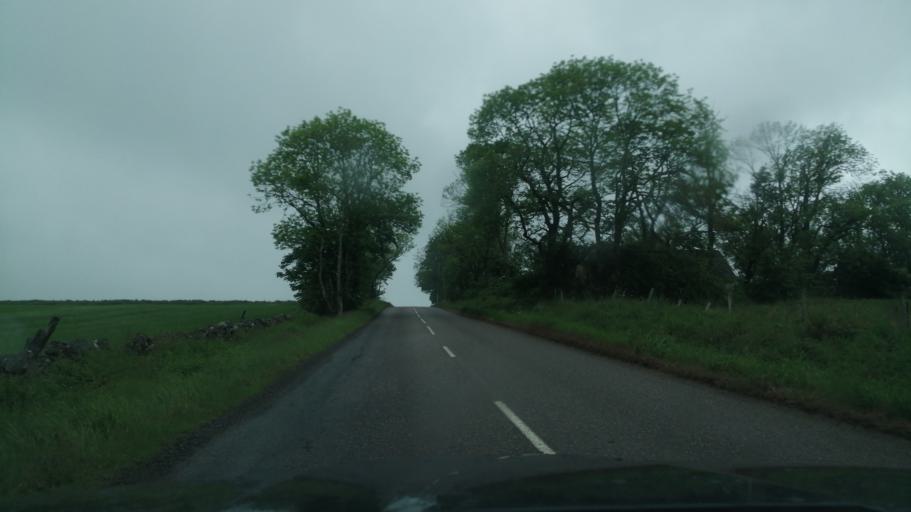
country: GB
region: Scotland
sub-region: Aberdeenshire
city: Huntly
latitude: 57.5459
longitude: -2.8129
